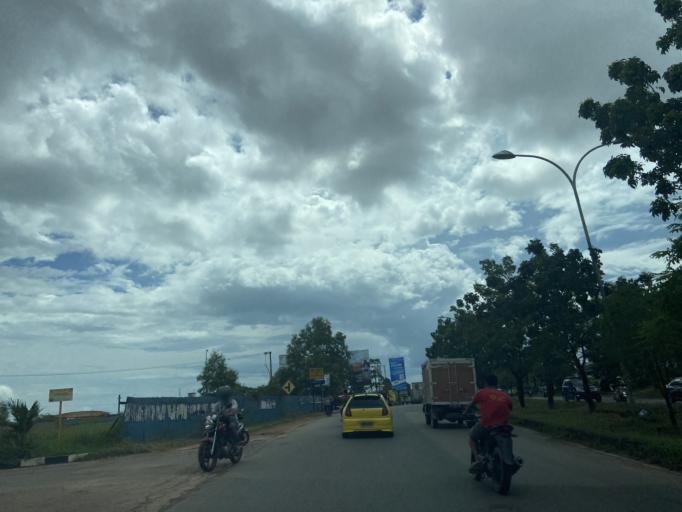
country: SG
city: Singapore
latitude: 1.0404
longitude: 103.9857
